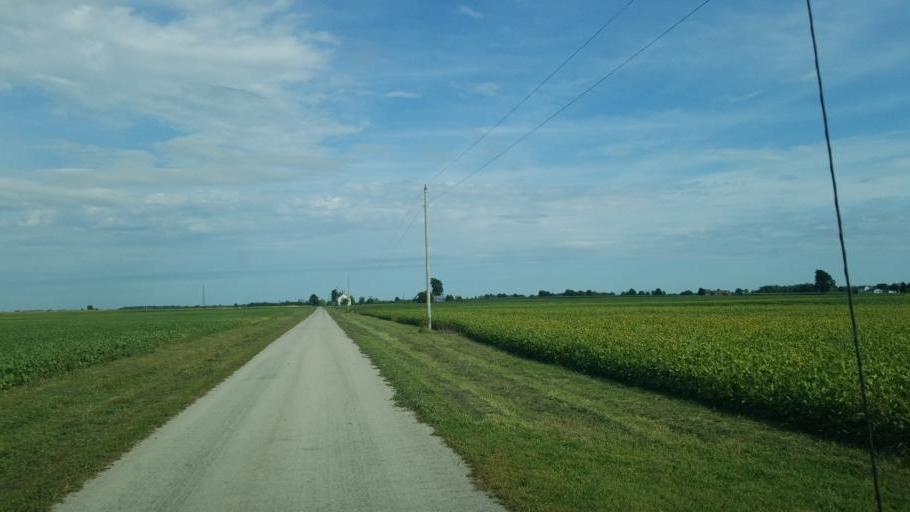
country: US
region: Ohio
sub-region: Hardin County
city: Forest
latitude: 40.8472
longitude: -83.4993
